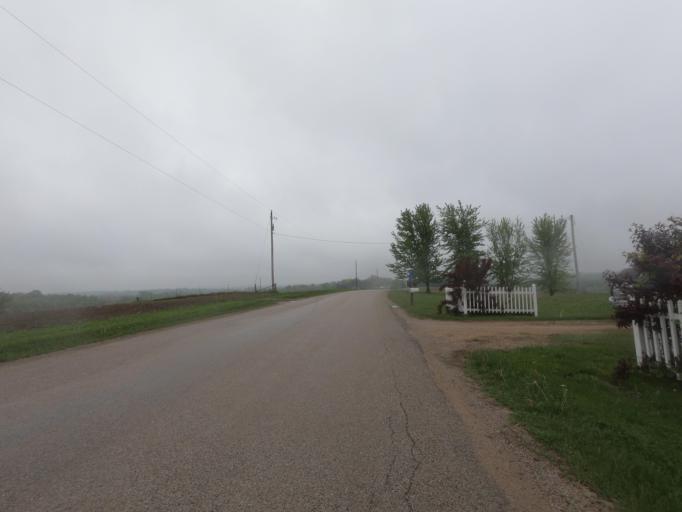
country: US
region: Wisconsin
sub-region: Grant County
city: Hazel Green
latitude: 42.4944
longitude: -90.4979
